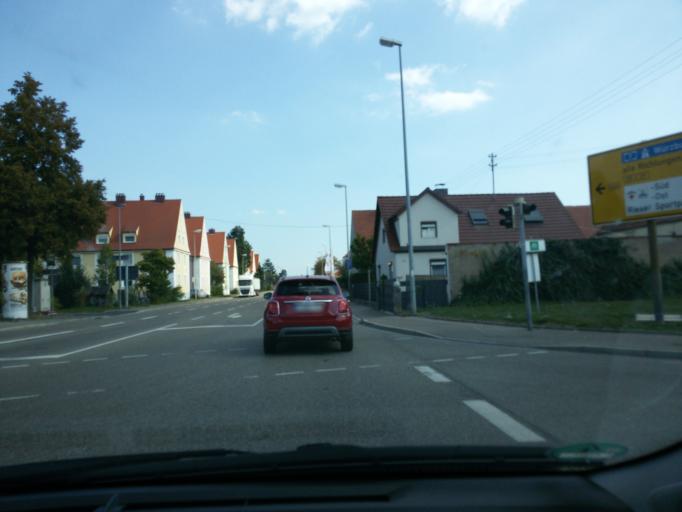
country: DE
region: Bavaria
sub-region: Swabia
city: Noerdlingen
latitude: 48.8464
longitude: 10.4976
